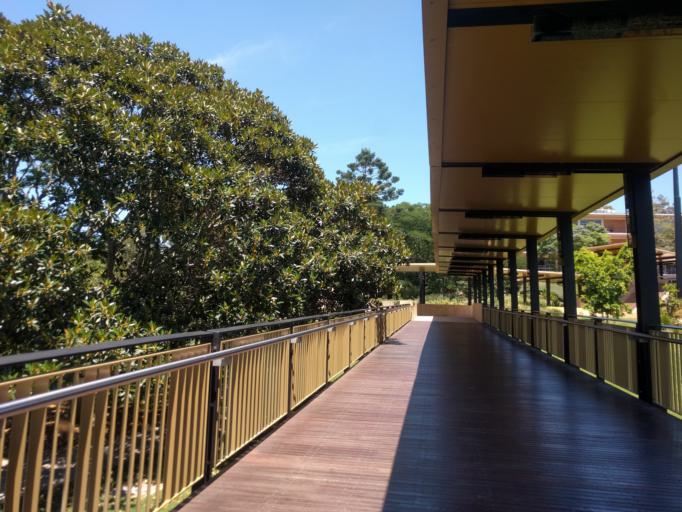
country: AU
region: Queensland
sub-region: Brisbane
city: South Brisbane
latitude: -27.4977
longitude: 153.0171
